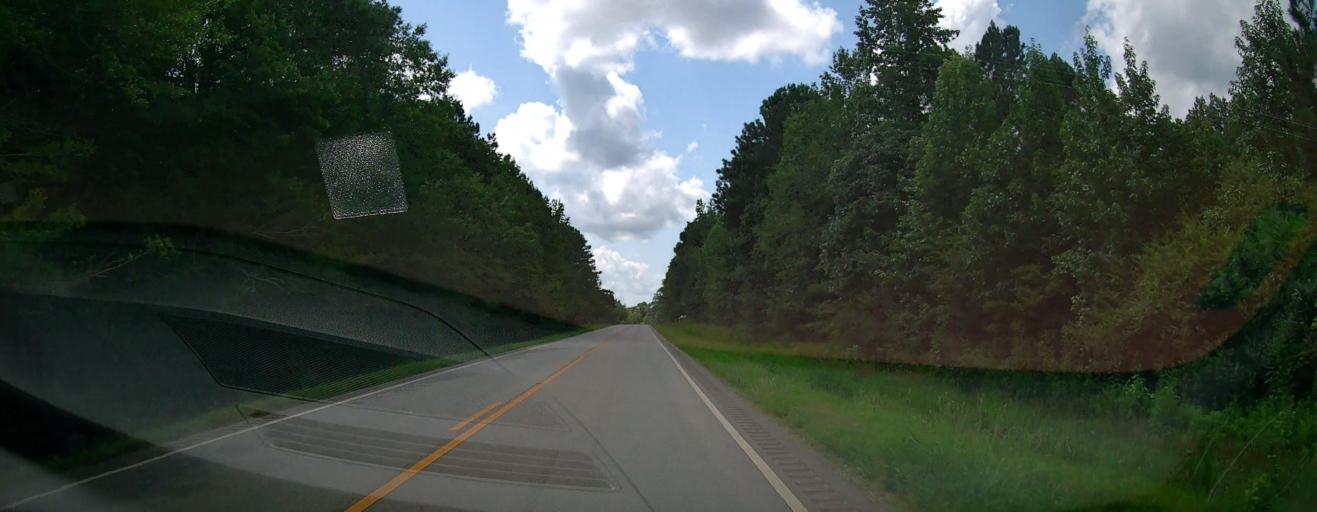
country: US
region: Alabama
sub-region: Cleburne County
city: Heflin
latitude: 33.5656
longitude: -85.4349
